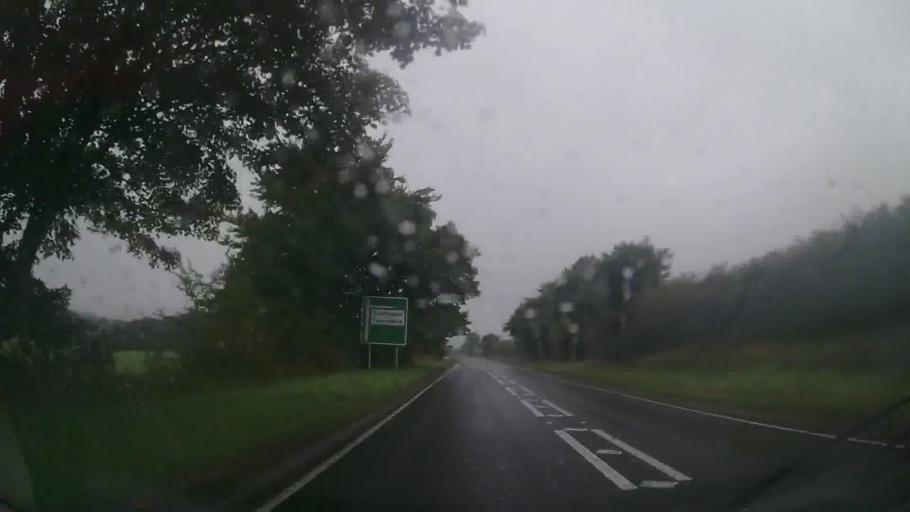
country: GB
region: Wales
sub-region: Carmarthenshire
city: Whitland
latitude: 51.7626
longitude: -4.6310
